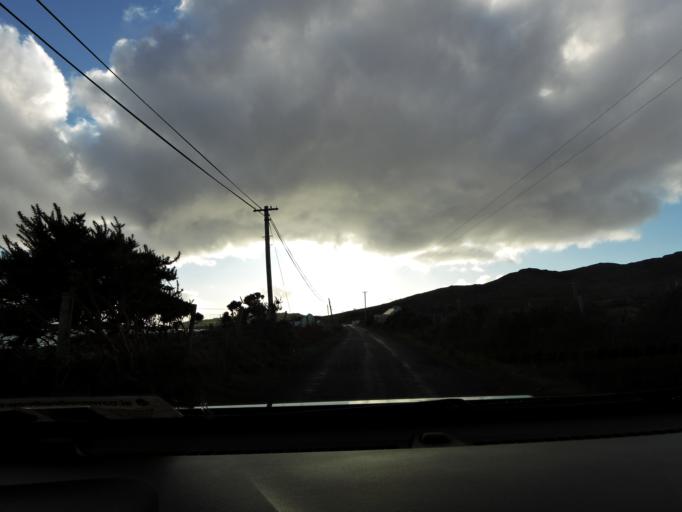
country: IE
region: Connaught
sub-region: Maigh Eo
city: Belmullet
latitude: 53.8898
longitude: -9.9422
